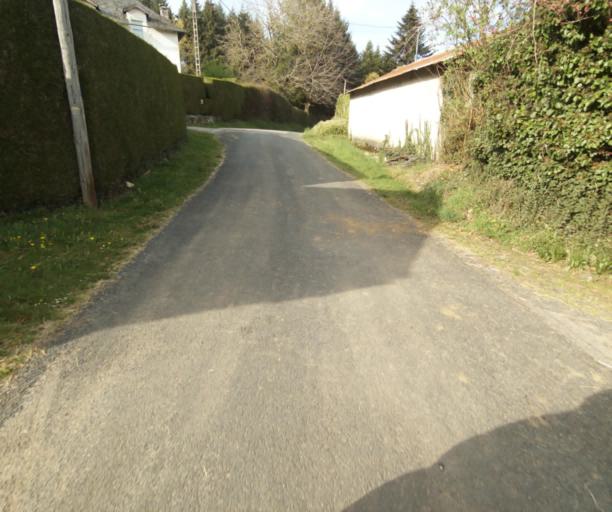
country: FR
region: Limousin
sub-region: Departement de la Correze
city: Naves
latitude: 45.3184
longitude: 1.7413
